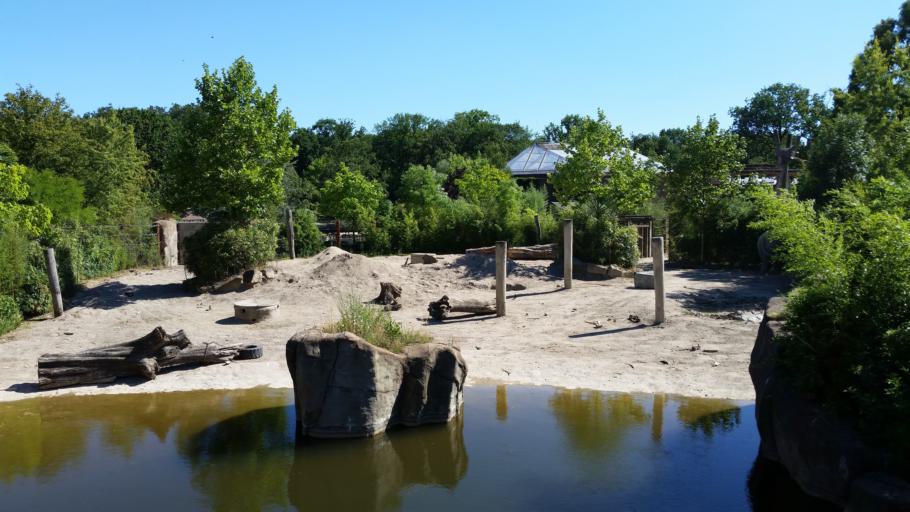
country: DE
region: North Rhine-Westphalia
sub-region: Regierungsbezirk Munster
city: Muenster
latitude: 51.9468
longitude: 7.5913
